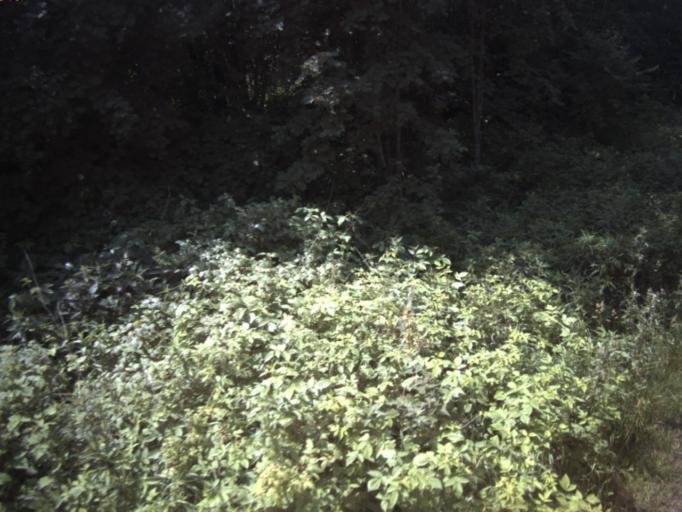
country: SE
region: Skane
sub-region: Angelholms Kommun
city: Strovelstorp
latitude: 56.1910
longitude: 12.7687
